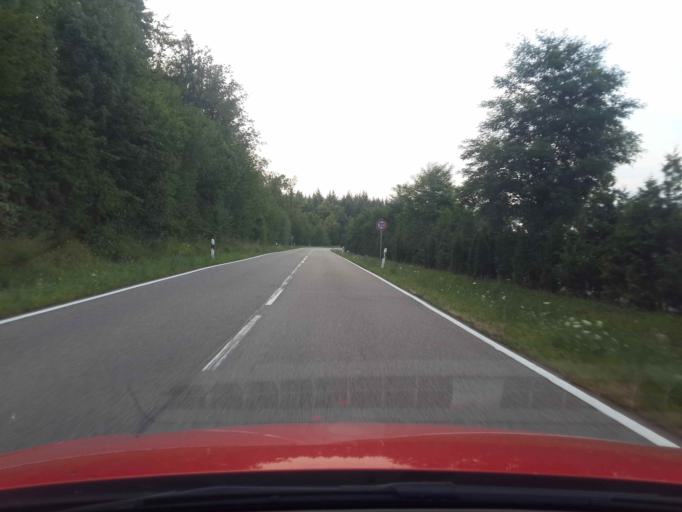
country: DE
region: Baden-Wuerttemberg
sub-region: Regierungsbezirk Stuttgart
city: Pfaffenhofen
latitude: 49.0448
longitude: 8.9867
